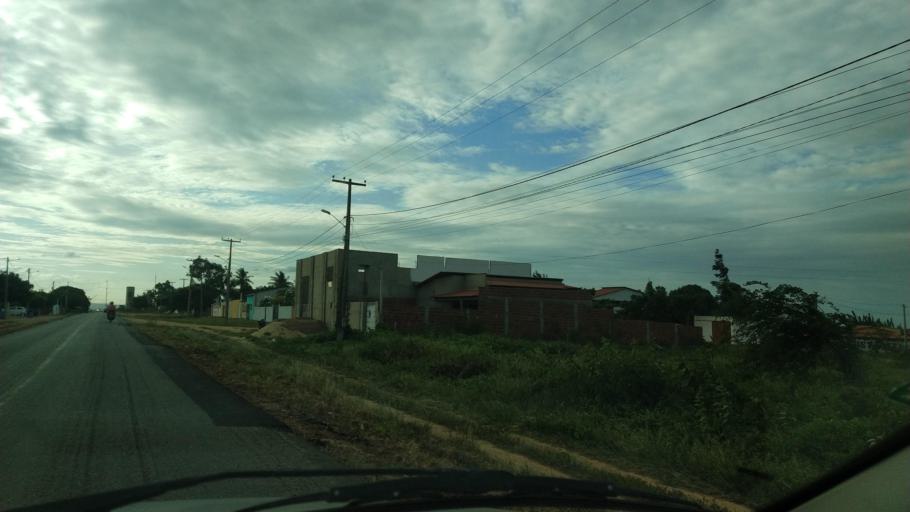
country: BR
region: Rio Grande do Norte
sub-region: Sao Paulo Do Potengi
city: Sao Paulo do Potengi
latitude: -5.9111
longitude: -35.7555
